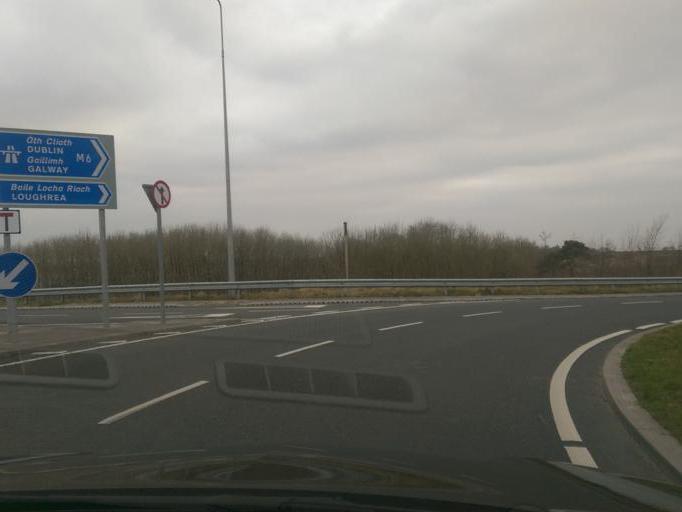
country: IE
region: Connaught
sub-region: County Galway
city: Athenry
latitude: 53.2900
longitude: -8.7558
